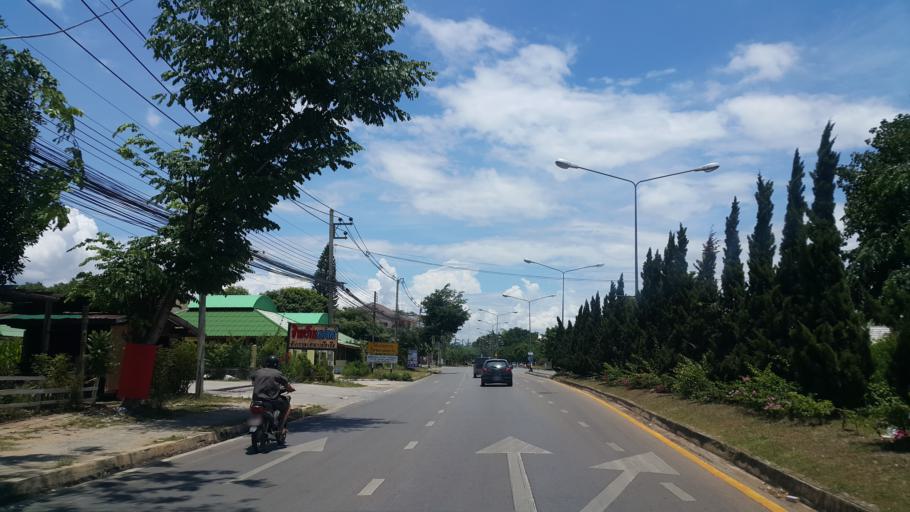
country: TH
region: Phayao
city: Phayao
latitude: 19.1801
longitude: 99.8850
